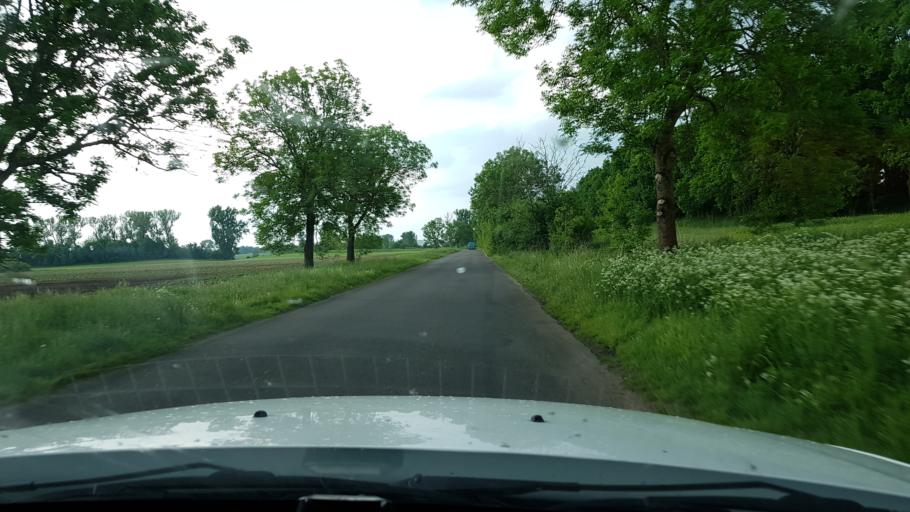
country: PL
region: West Pomeranian Voivodeship
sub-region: Powiat stargardzki
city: Marianowo
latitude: 53.3265
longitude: 15.1858
